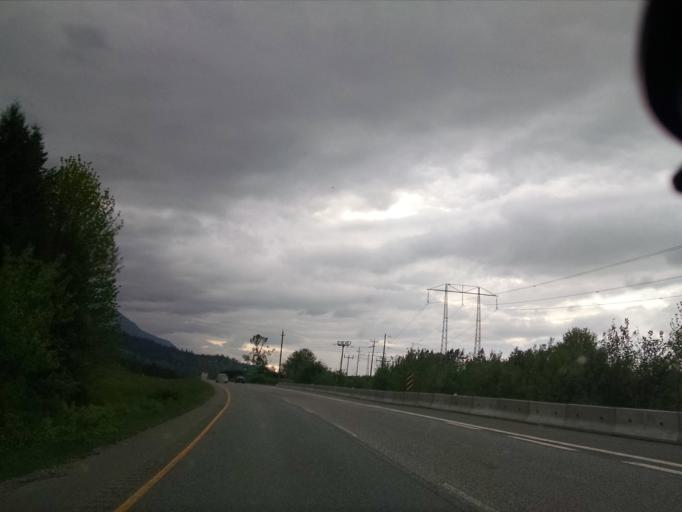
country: CA
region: British Columbia
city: Agassiz
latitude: 49.1954
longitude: -121.7346
